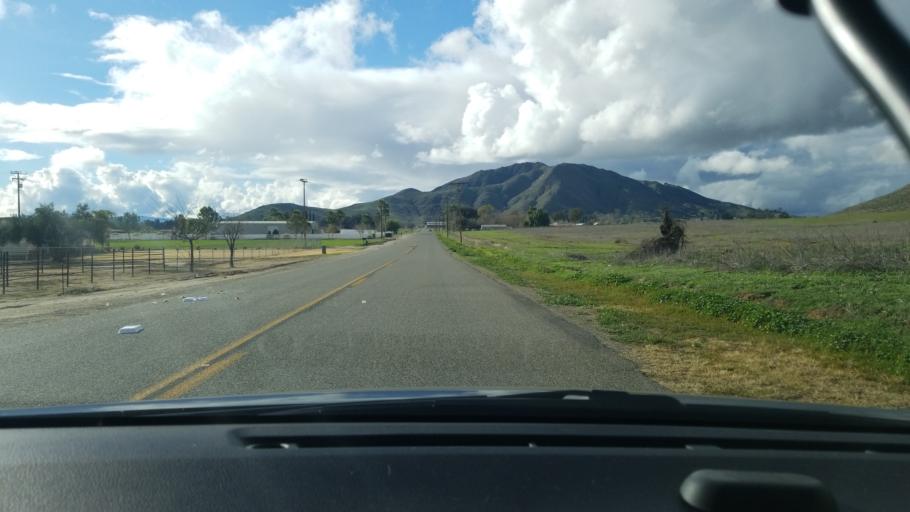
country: US
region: California
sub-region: Riverside County
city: Green Acres
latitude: 33.7220
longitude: -117.0588
